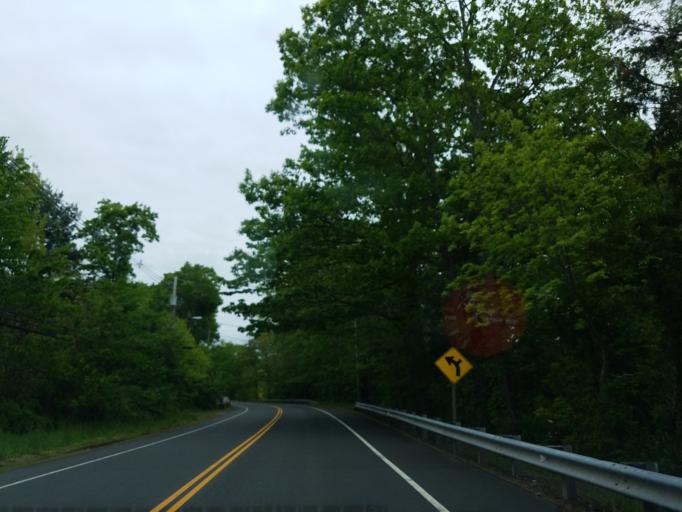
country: US
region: Connecticut
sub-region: New Haven County
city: Wallingford Center
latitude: 41.4143
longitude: -72.7494
